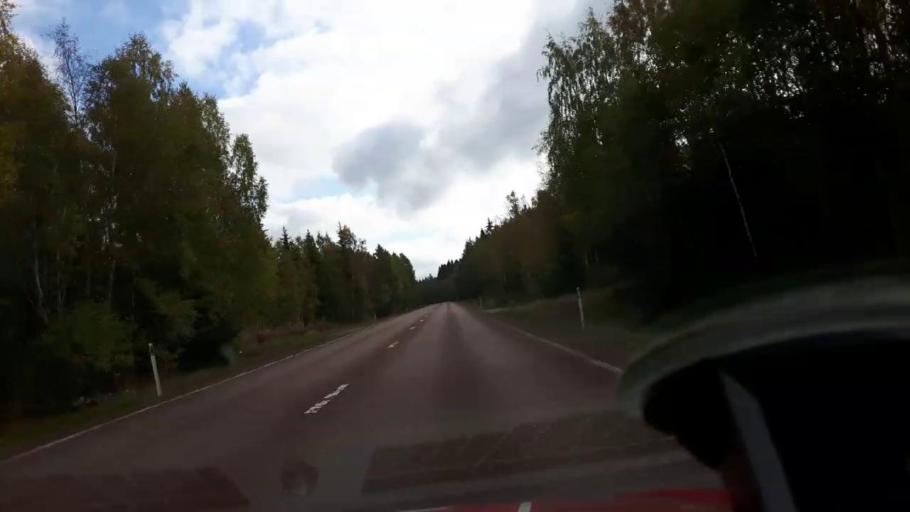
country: SE
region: Gaevleborg
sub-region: Ljusdals Kommun
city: Jaervsoe
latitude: 61.6407
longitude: 16.2330
